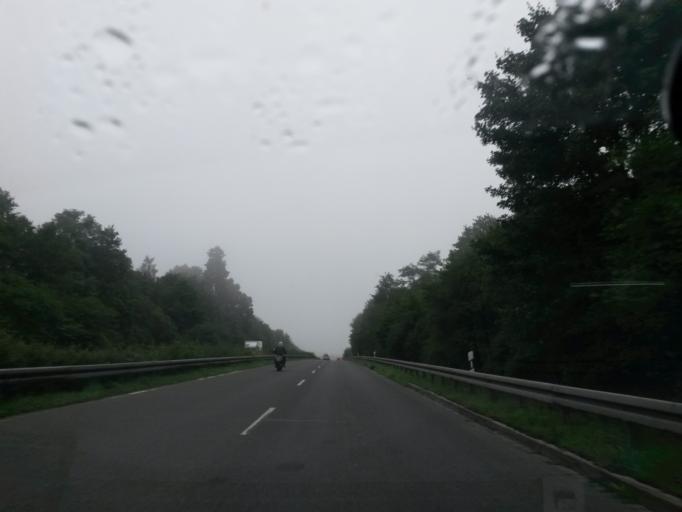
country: DE
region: Bavaria
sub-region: Regierungsbezirk Mittelfranken
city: Zirndorf
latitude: 49.4473
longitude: 10.9750
